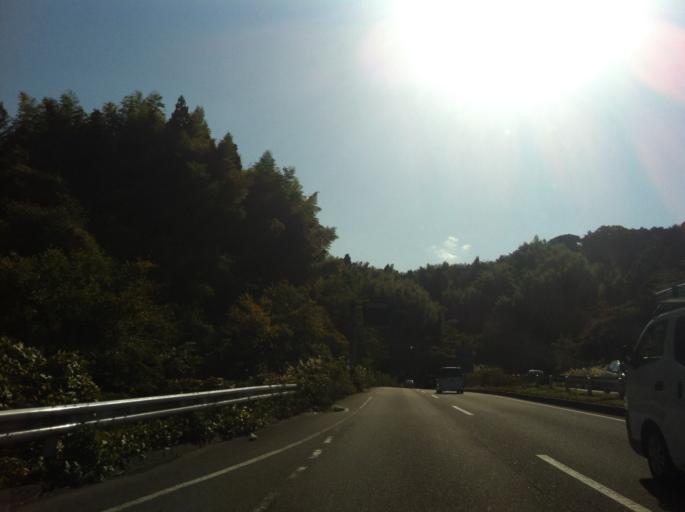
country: JP
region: Shizuoka
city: Yaizu
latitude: 34.9204
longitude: 138.2917
